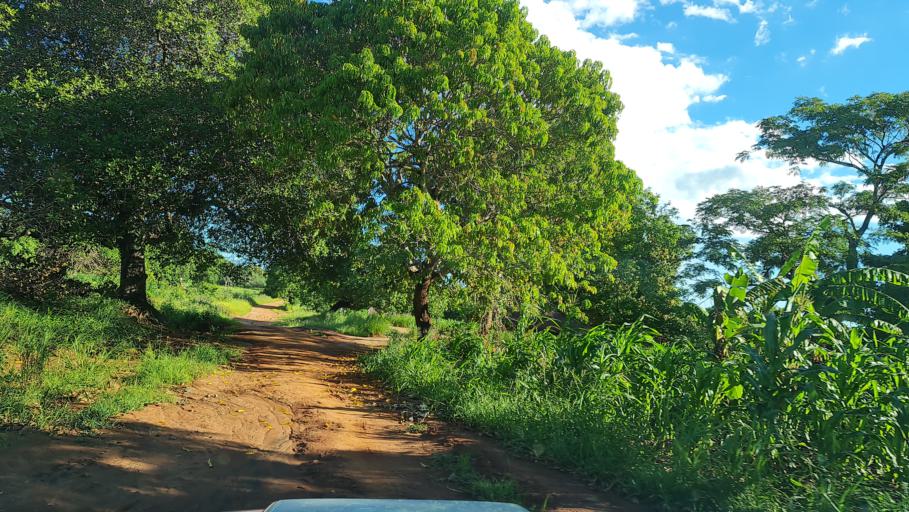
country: MZ
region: Nampula
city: Ilha de Mocambique
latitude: -14.9239
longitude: 40.2189
